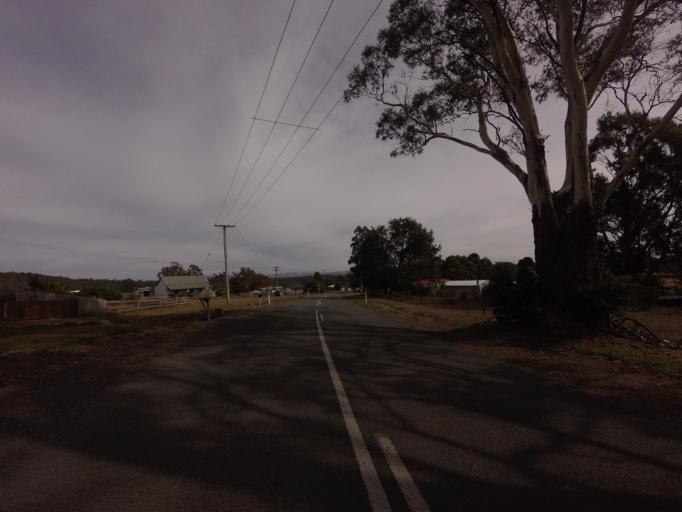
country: AU
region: Tasmania
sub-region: Brighton
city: Bridgewater
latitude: -42.3585
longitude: 147.4081
